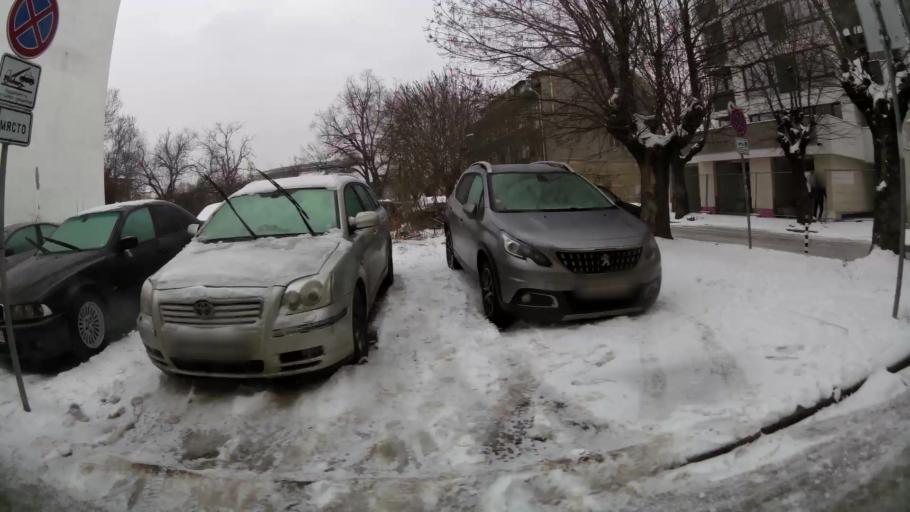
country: BG
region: Sofia-Capital
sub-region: Stolichna Obshtina
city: Sofia
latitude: 42.7112
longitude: 23.3174
